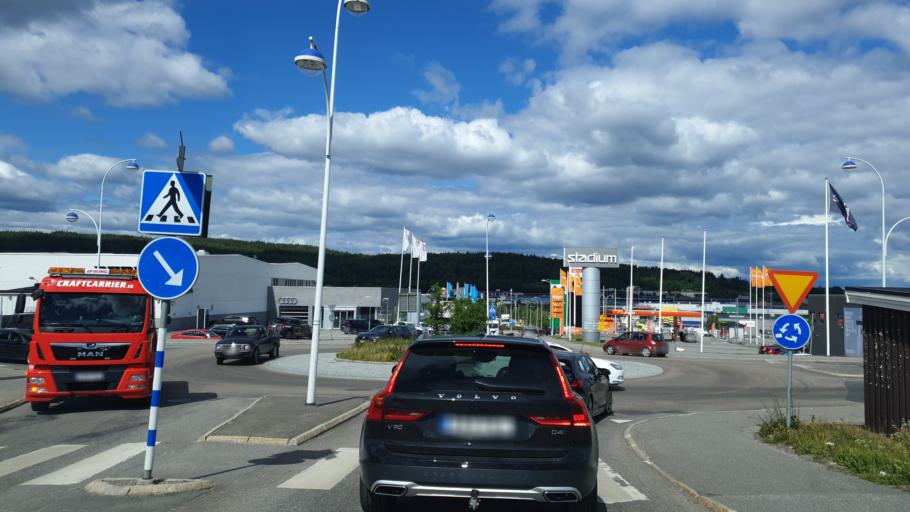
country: SE
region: Vaesternorrland
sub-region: Sundsvalls Kommun
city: Sundsbruk
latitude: 62.4415
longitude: 17.3316
